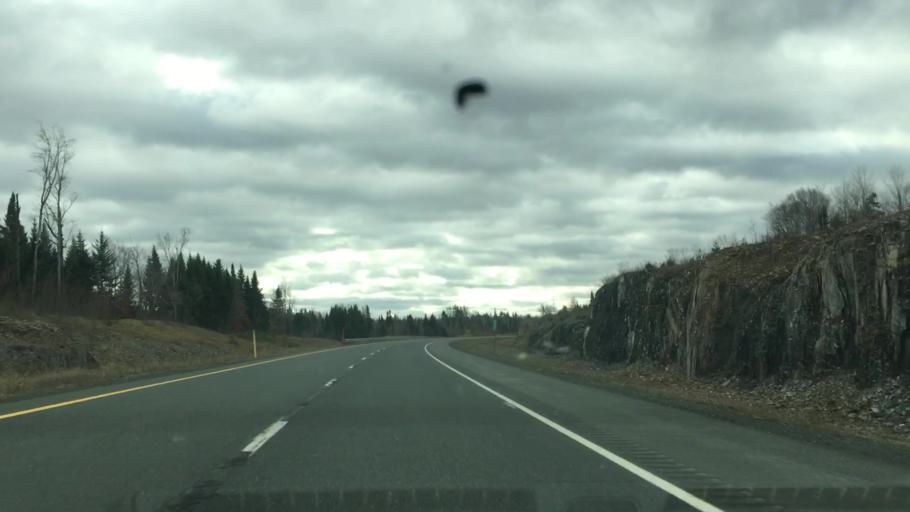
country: US
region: Maine
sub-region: Aroostook County
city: Easton
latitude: 46.6209
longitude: -67.7387
